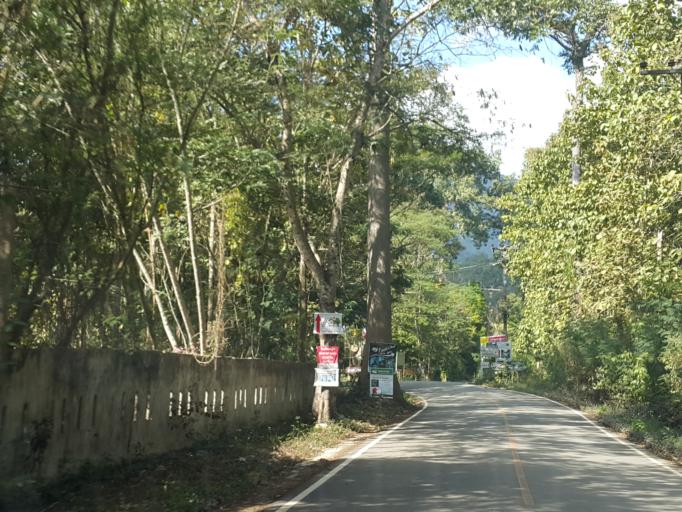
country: TH
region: Chiang Mai
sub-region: Amphoe Chiang Dao
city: Chiang Dao
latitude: 19.4012
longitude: 98.9287
